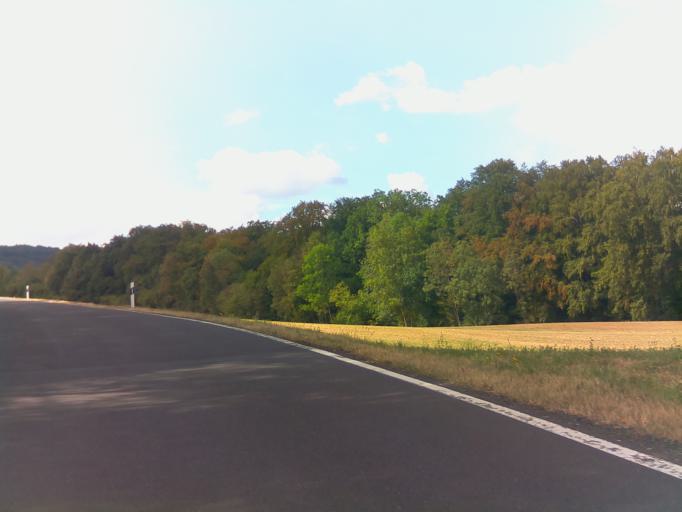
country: DE
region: Bavaria
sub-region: Regierungsbezirk Unterfranken
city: Oberelsbach
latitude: 50.4637
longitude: 10.1157
